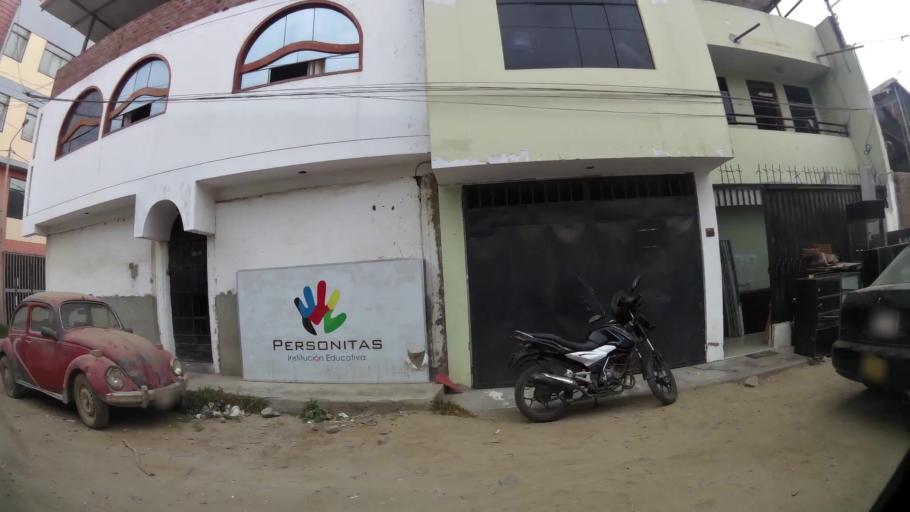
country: PE
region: La Libertad
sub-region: Provincia de Trujillo
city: Trujillo
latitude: -8.1148
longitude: -79.0471
